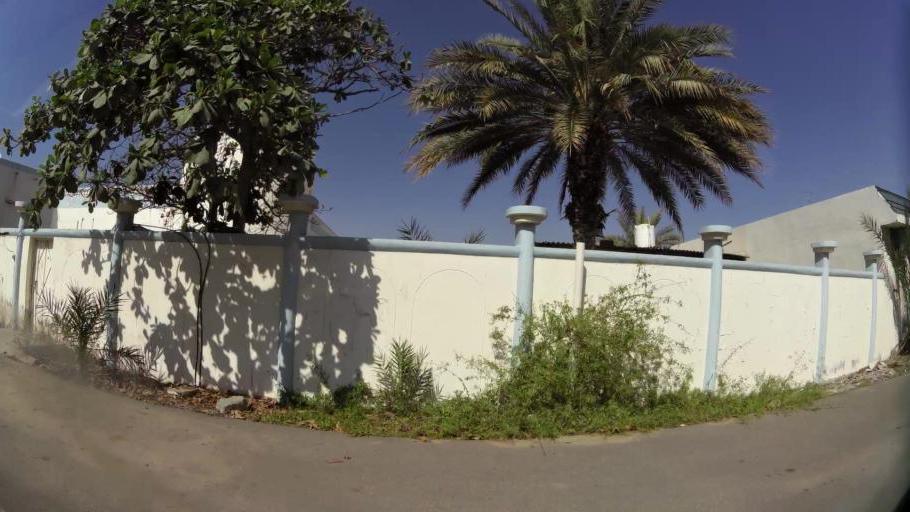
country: AE
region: Ajman
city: Ajman
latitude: 25.4160
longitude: 55.4647
